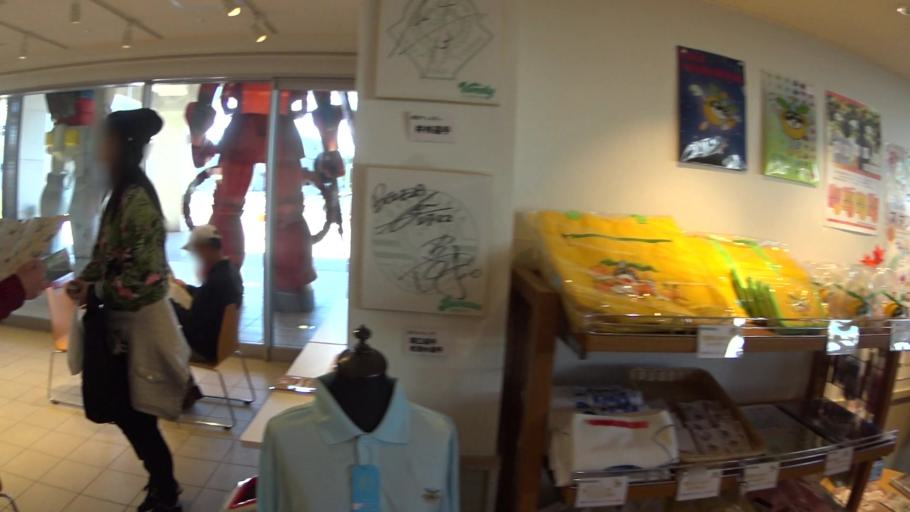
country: JP
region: Tokyo
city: Chofugaoka
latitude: 35.6441
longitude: 139.5028
